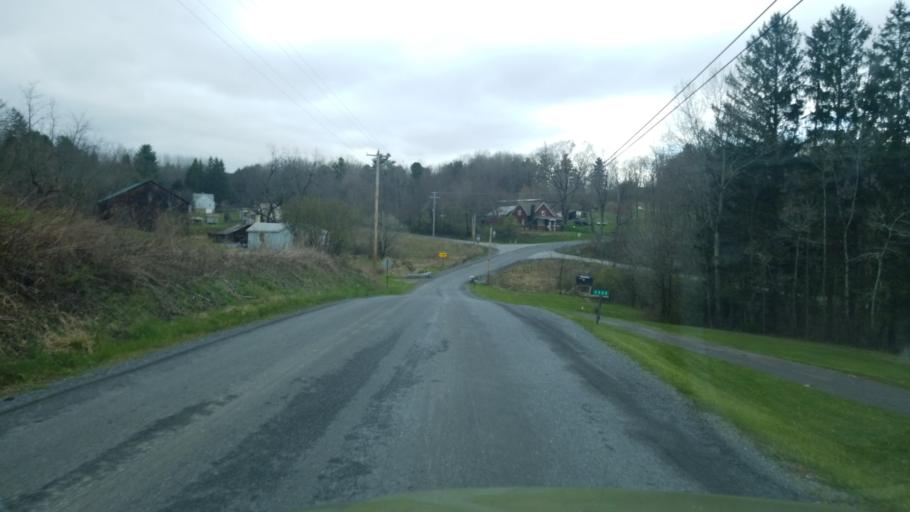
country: US
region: Pennsylvania
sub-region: Clearfield County
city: Clearfield
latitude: 41.0823
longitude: -78.4089
